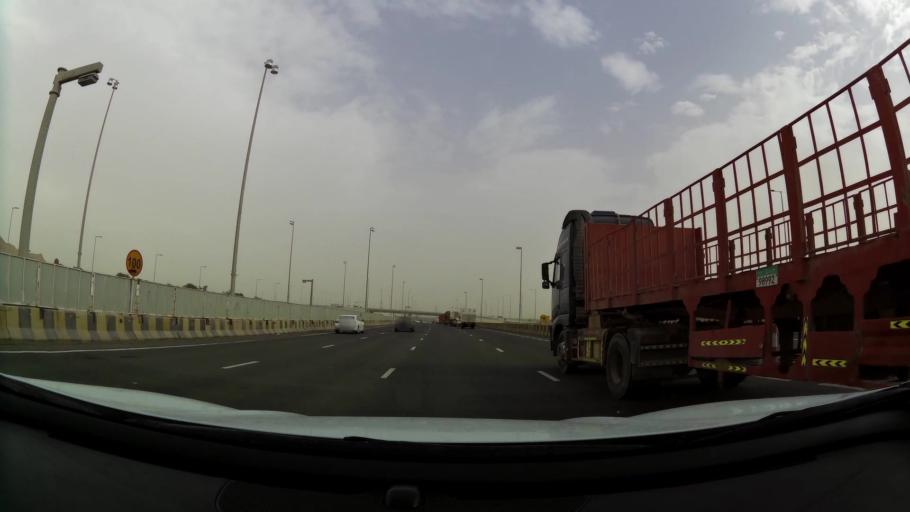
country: AE
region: Abu Dhabi
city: Abu Dhabi
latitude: 24.4603
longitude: 54.6278
